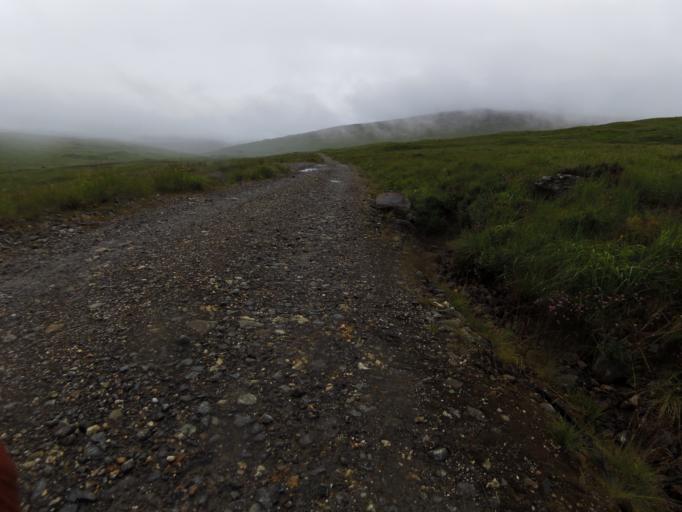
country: GB
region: Scotland
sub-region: Highland
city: Spean Bridge
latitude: 56.7705
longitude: -4.6983
